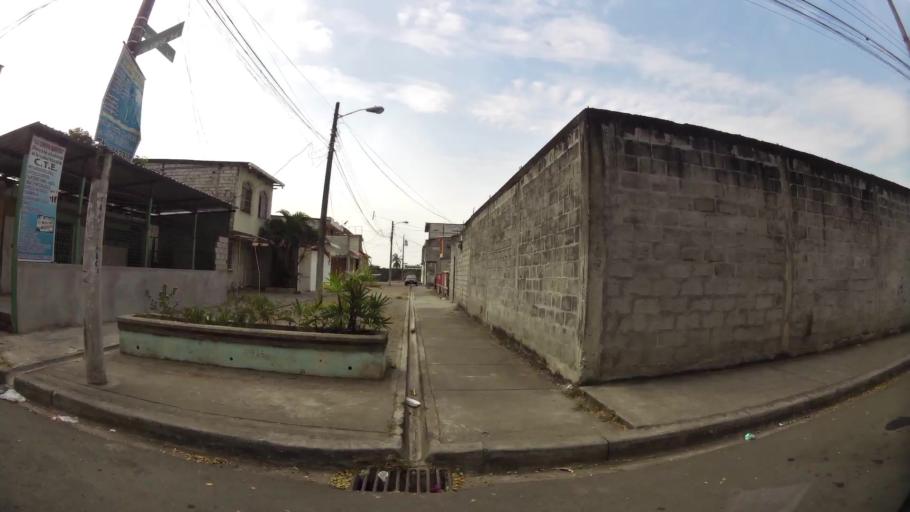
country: EC
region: Guayas
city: Guayaquil
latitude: -2.2607
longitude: -79.8993
